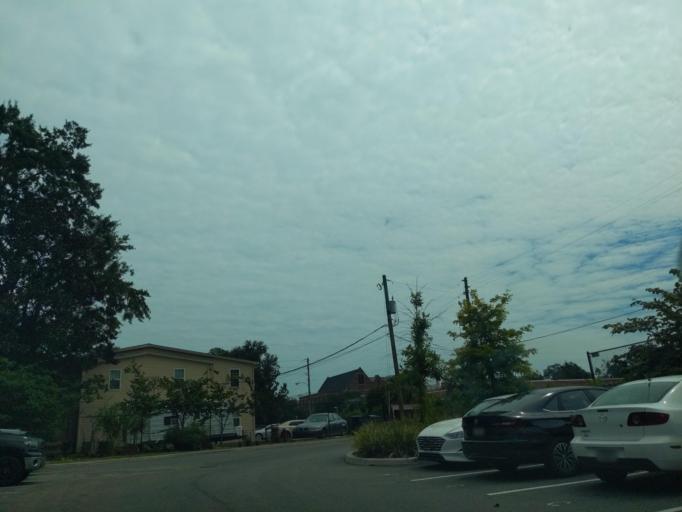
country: US
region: Florida
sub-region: Leon County
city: Tallahassee
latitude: 30.4456
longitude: -84.3086
